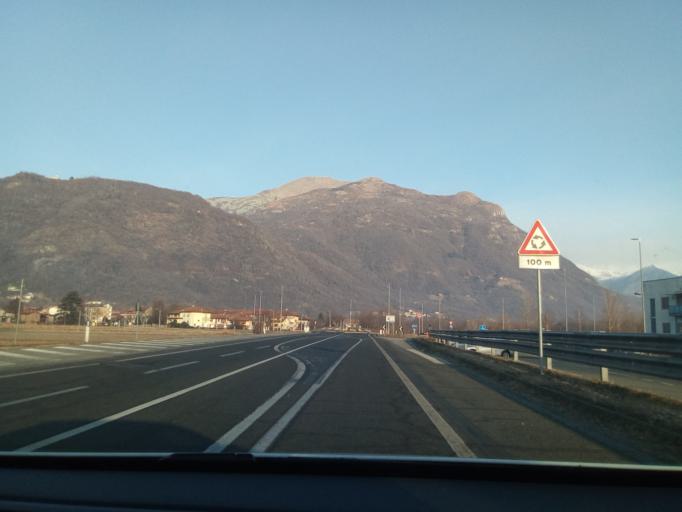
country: IT
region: Piedmont
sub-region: Provincia di Torino
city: Fiorano Canavese
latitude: 45.4785
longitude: 7.8315
